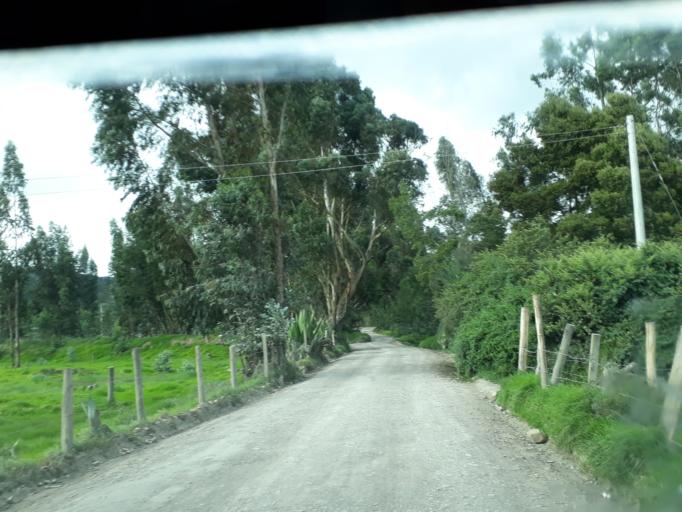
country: CO
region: Cundinamarca
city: Cucunuba
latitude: 5.2604
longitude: -73.7745
